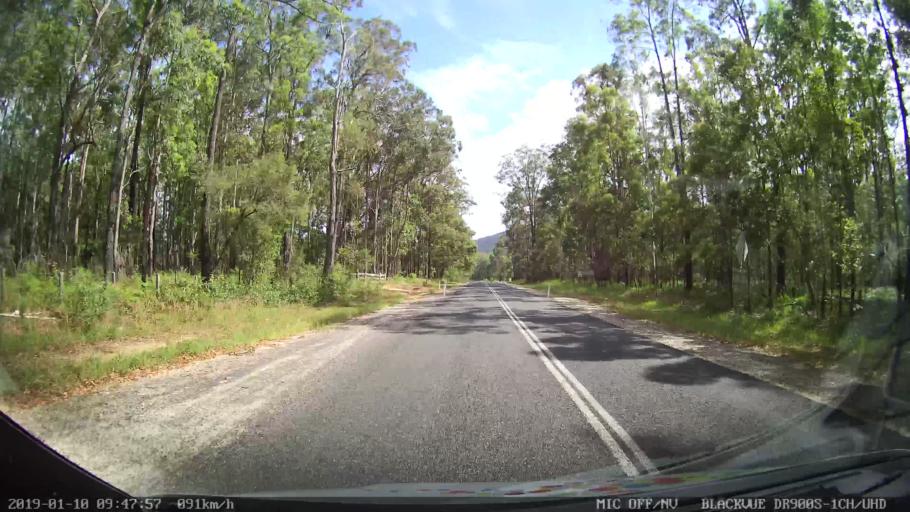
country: AU
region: New South Wales
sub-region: Coffs Harbour
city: Nana Glen
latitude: -30.0788
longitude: 152.9889
